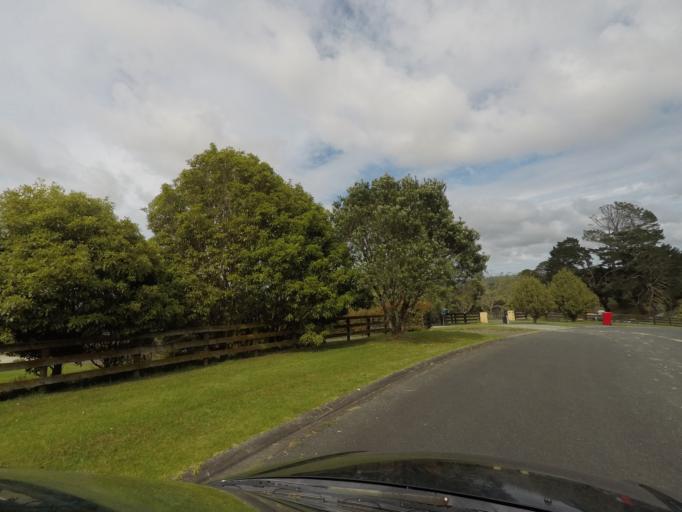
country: NZ
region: Auckland
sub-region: Auckland
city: Muriwai Beach
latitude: -36.7592
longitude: 174.5619
